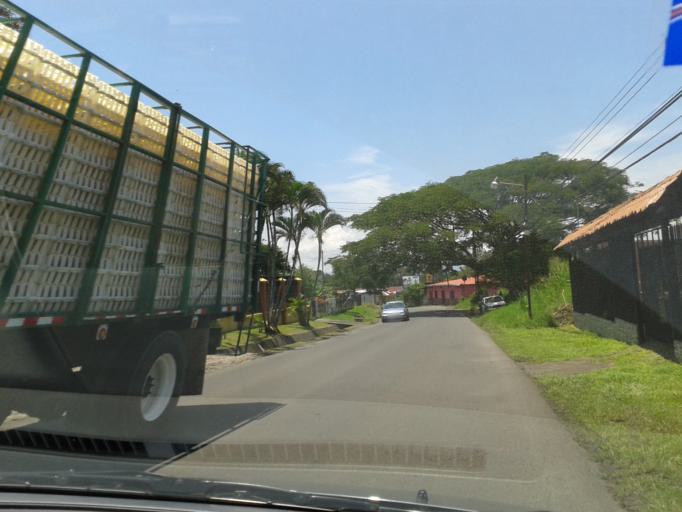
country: CR
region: Alajuela
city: Alajuela
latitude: 10.0064
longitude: -84.2294
